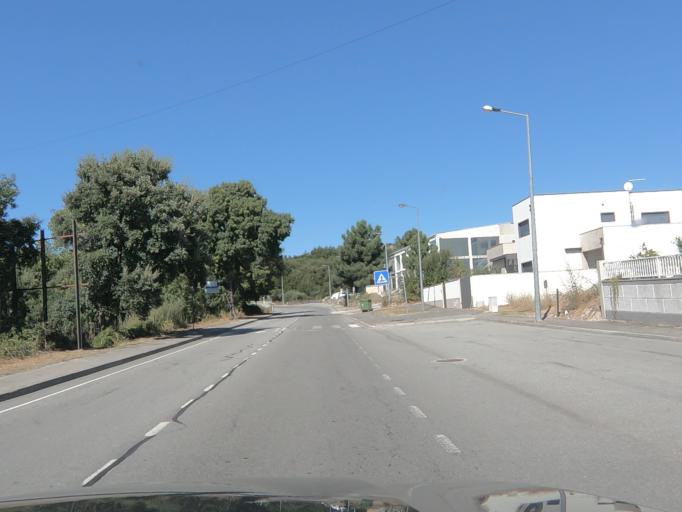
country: PT
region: Vila Real
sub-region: Valpacos
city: Valpacos
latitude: 41.6277
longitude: -7.3129
